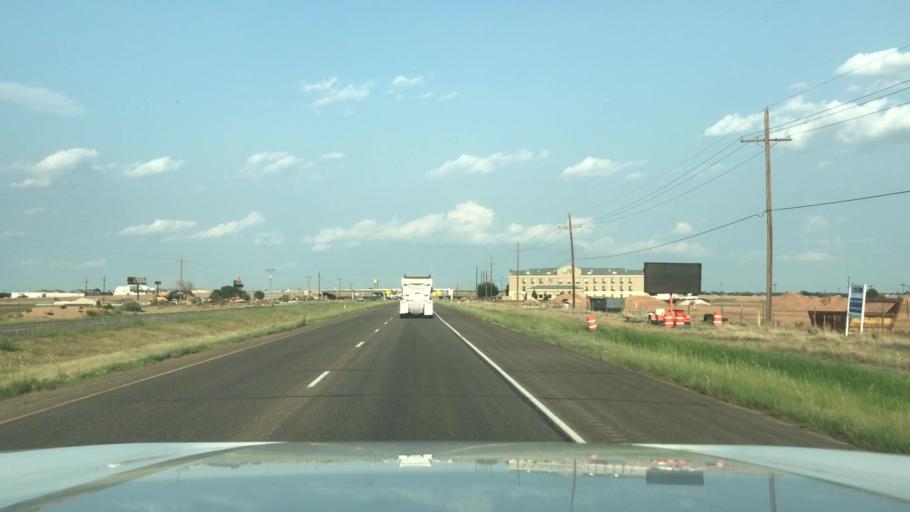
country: US
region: Texas
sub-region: Potter County
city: Amarillo
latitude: 35.1167
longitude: -101.9165
